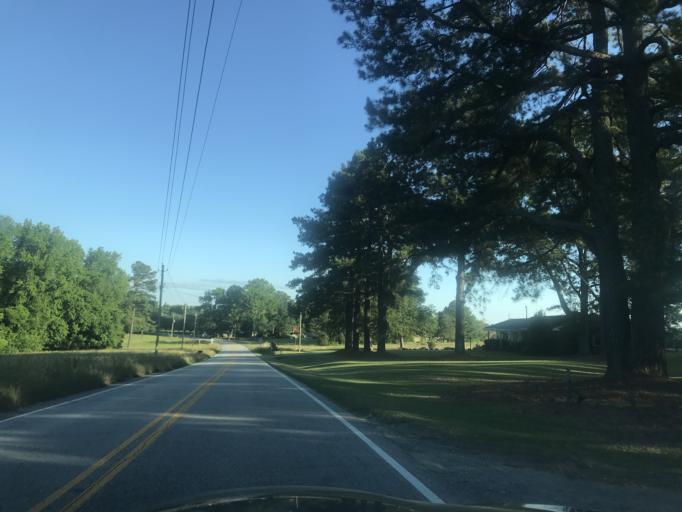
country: US
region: North Carolina
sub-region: Johnston County
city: Archer Lodge
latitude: 35.7049
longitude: -78.3855
